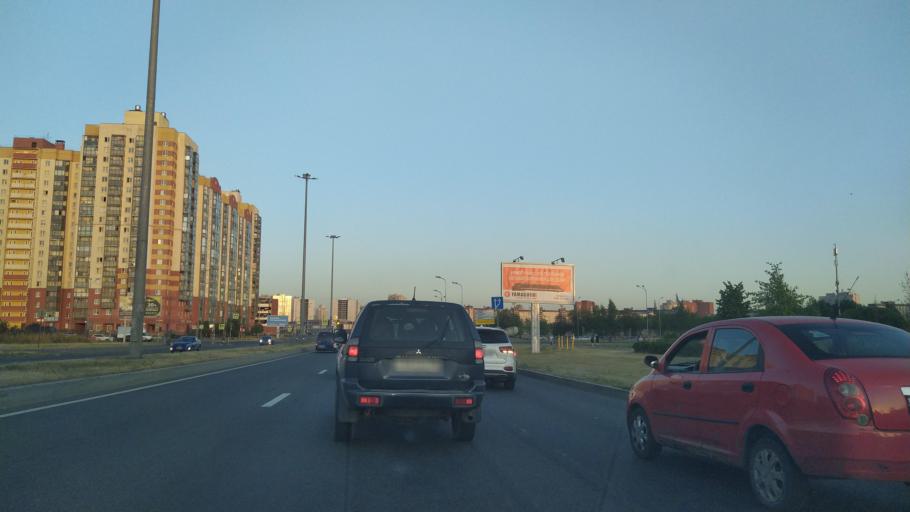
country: RU
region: St.-Petersburg
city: Komendantsky aerodrom
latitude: 60.0222
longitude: 30.2630
